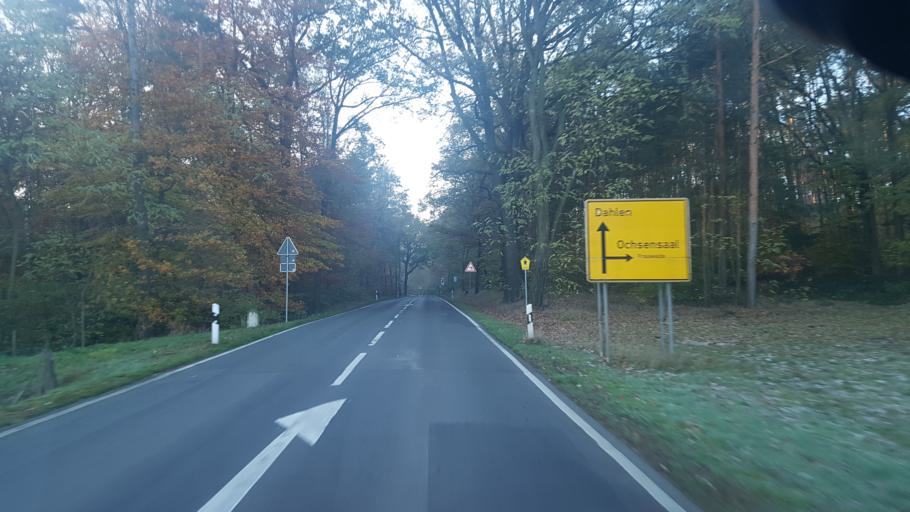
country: DE
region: Saxony
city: Schildau
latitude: 51.4265
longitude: 12.9708
